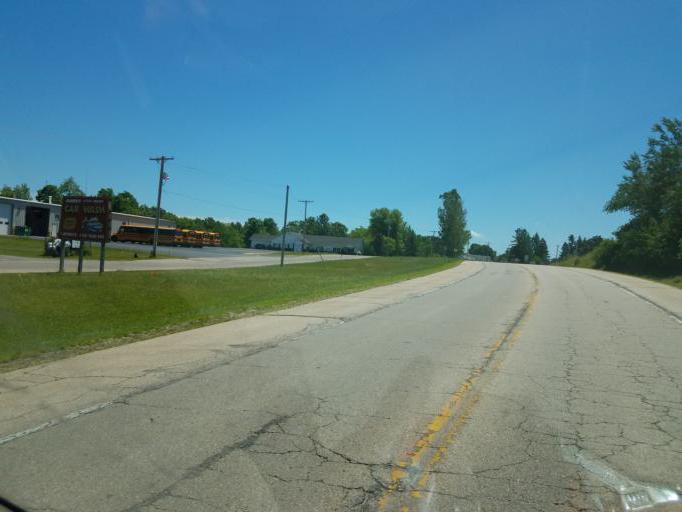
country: US
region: Wisconsin
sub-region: Juneau County
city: Elroy
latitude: 43.7572
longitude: -90.2739
